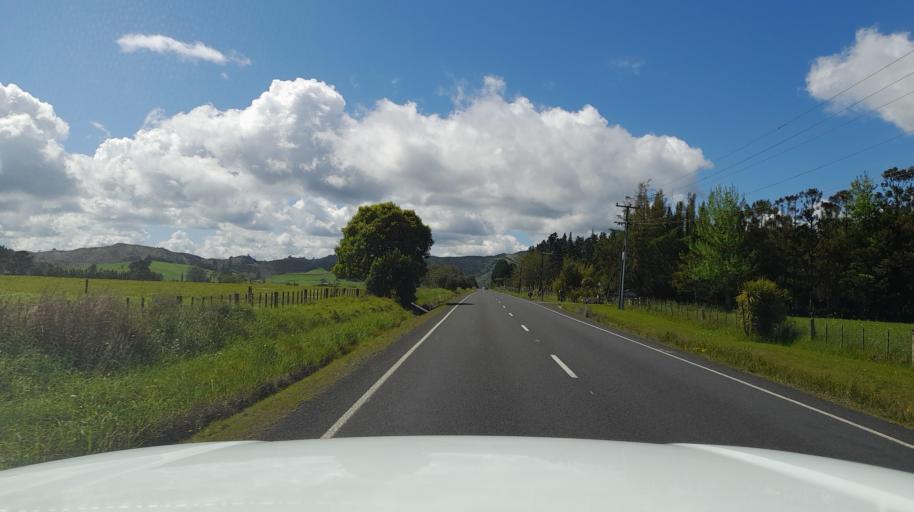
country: NZ
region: Northland
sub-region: Far North District
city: Taipa
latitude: -35.0281
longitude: 173.4803
